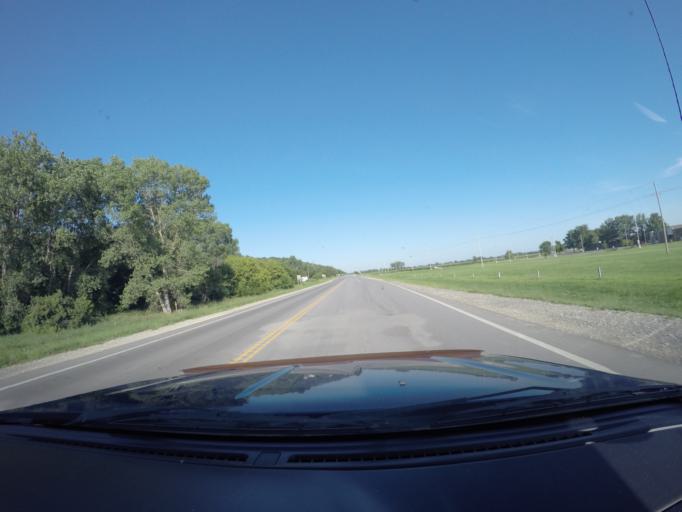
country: US
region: Kansas
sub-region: Jefferson County
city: Oskaloosa
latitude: 39.0796
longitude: -95.3839
